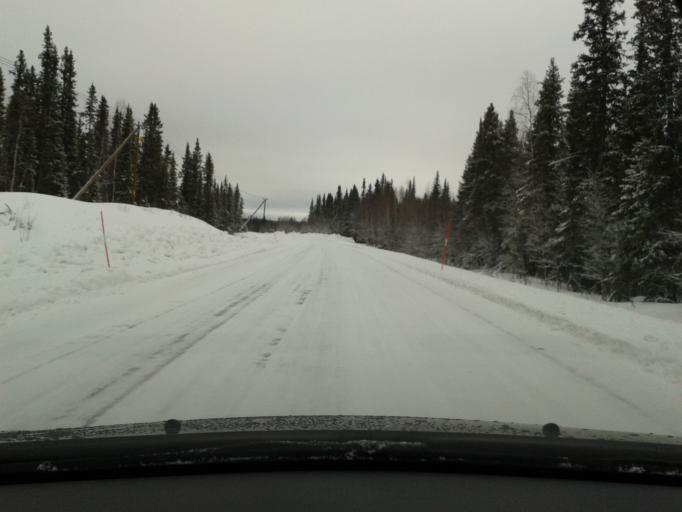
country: SE
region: Vaesterbotten
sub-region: Vilhelmina Kommun
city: Sjoberg
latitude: 65.2248
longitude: 15.9380
